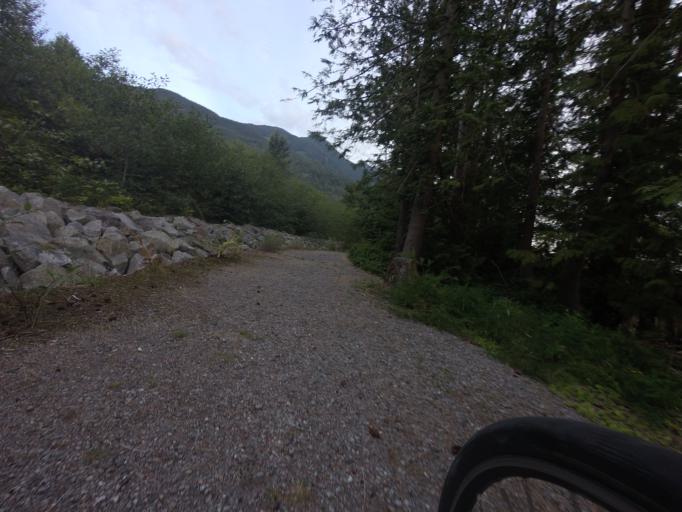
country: CA
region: British Columbia
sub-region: Greater Vancouver Regional District
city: Lions Bay
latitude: 49.5809
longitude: -123.2273
